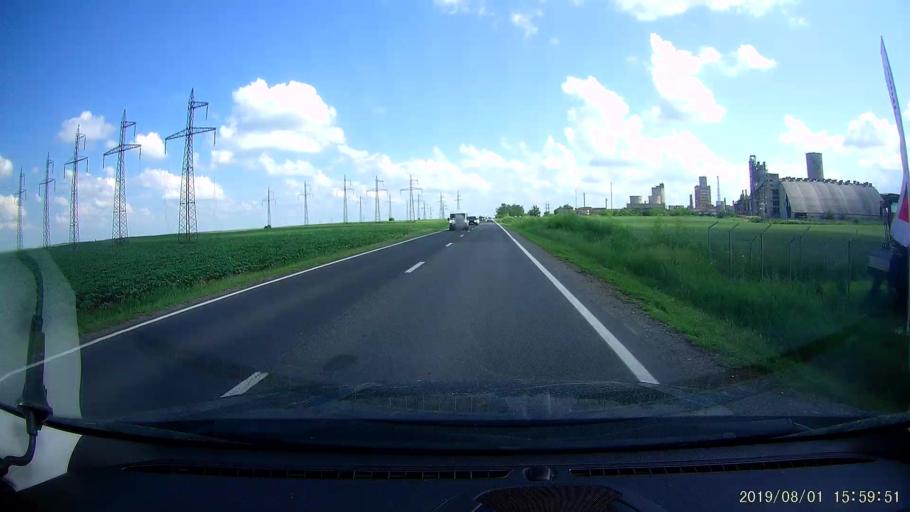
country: RO
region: Ialomita
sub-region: Comuna Slobozia
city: Slobozia
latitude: 44.5397
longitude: 27.3864
